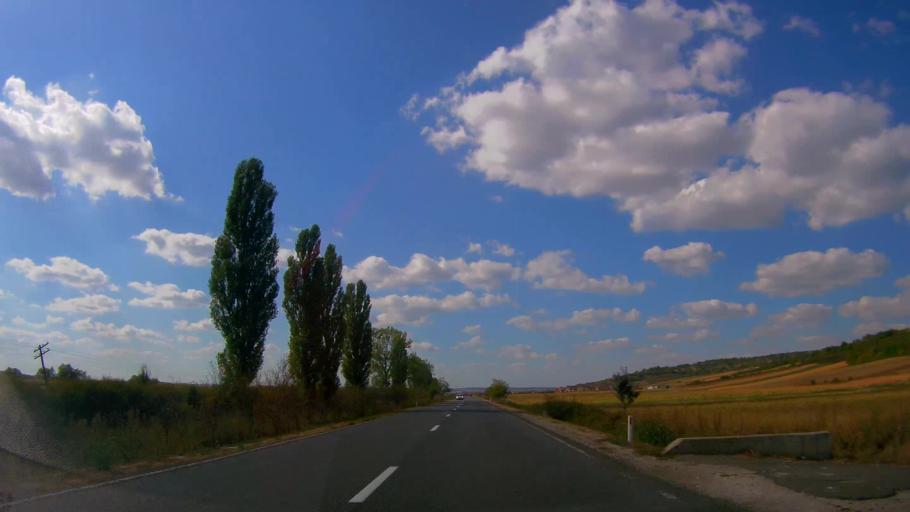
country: RO
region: Salaj
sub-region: Comuna Sarmasag
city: Sarmasag
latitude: 47.3319
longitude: 22.8557
